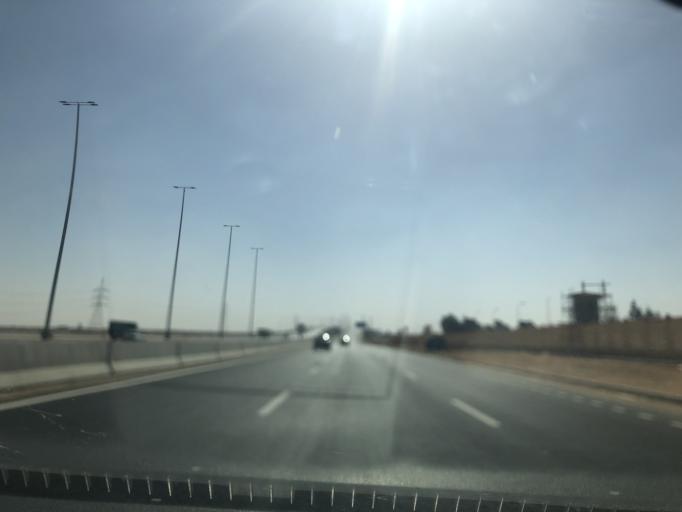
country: EG
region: Al Jizah
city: Madinat Sittah Uktubar
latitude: 29.8819
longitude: 31.0781
